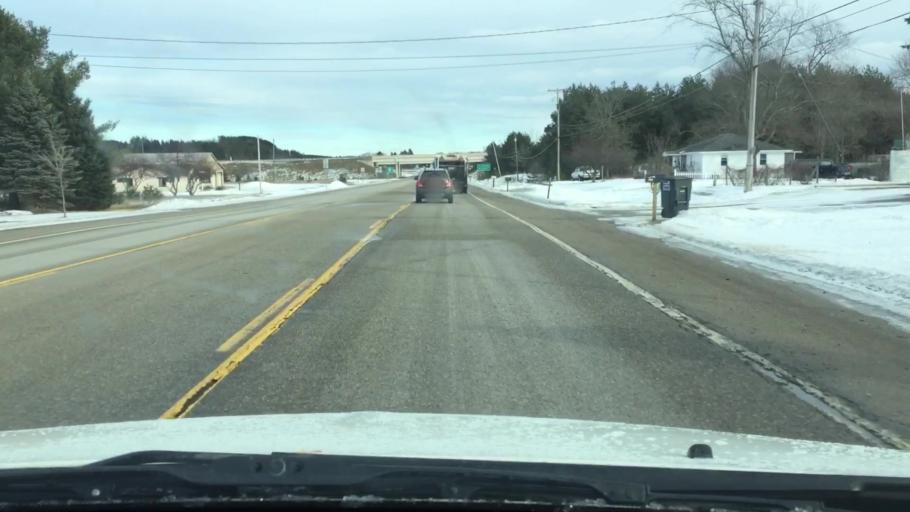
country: US
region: Michigan
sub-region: Wexford County
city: Manton
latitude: 44.4037
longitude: -85.3875
